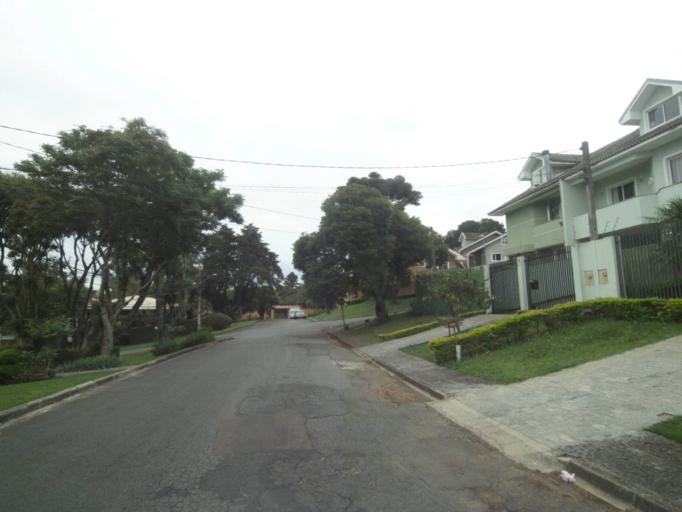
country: BR
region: Parana
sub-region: Pinhais
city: Pinhais
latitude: -25.4121
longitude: -49.2091
